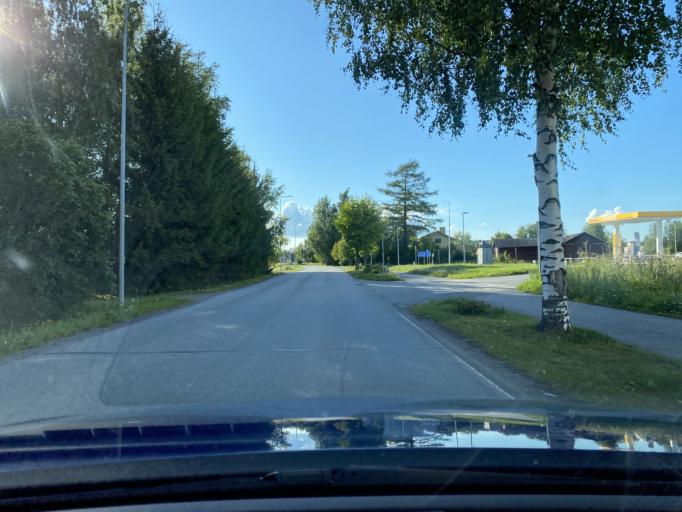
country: FI
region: Ostrobothnia
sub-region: Kyroenmaa
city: Laihia
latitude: 62.9824
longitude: 22.0016
